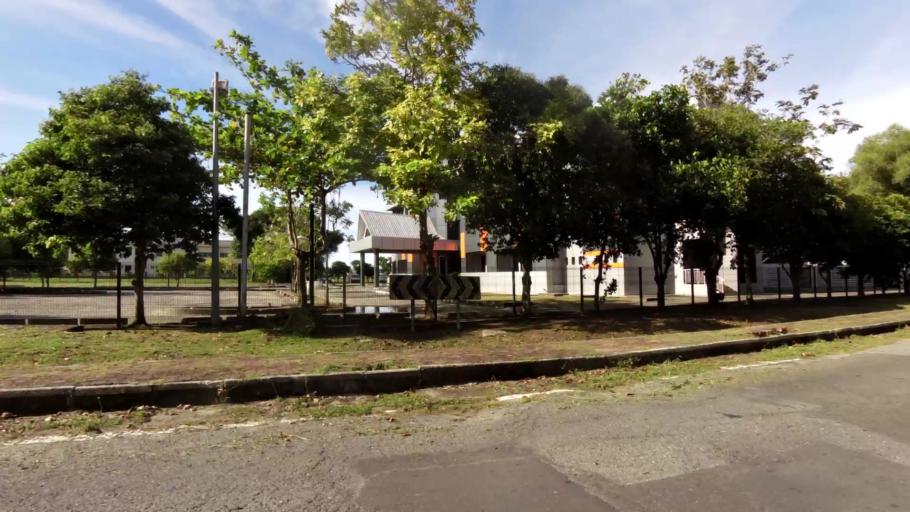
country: BN
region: Belait
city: Kuala Belait
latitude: 4.5866
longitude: 114.1938
